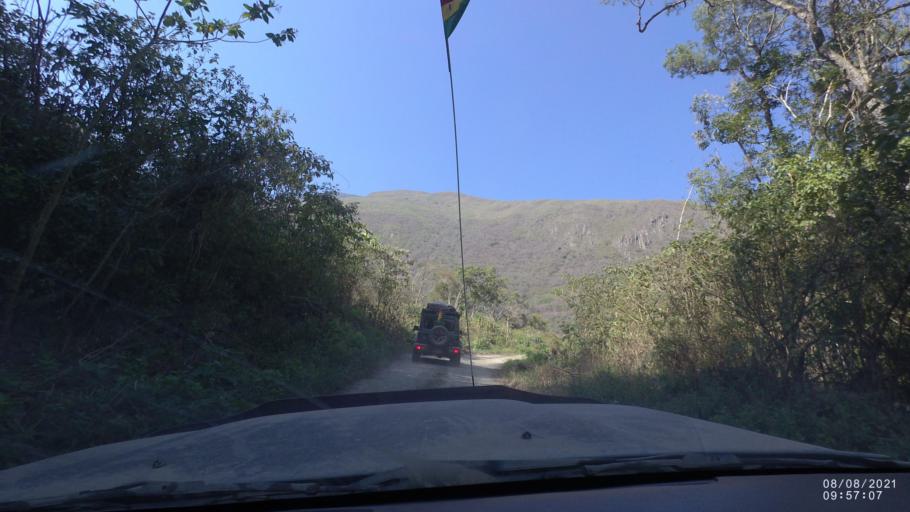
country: BO
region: La Paz
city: Quime
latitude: -16.6403
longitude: -66.7245
